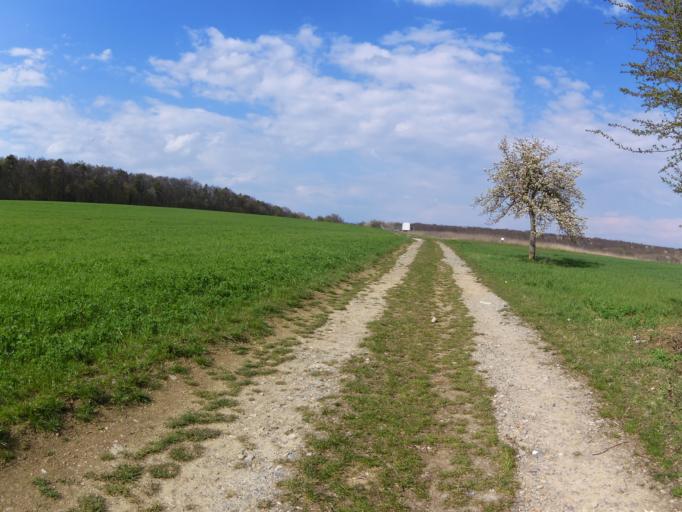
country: DE
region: Bavaria
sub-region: Regierungsbezirk Unterfranken
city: Rimpar
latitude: 49.8699
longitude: 9.9599
